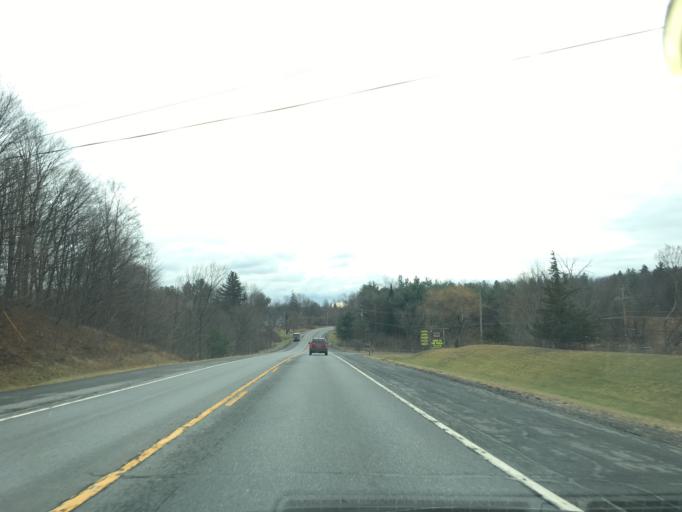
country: US
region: New York
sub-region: Rensselaer County
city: Poestenkill
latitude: 42.6623
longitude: -73.5774
